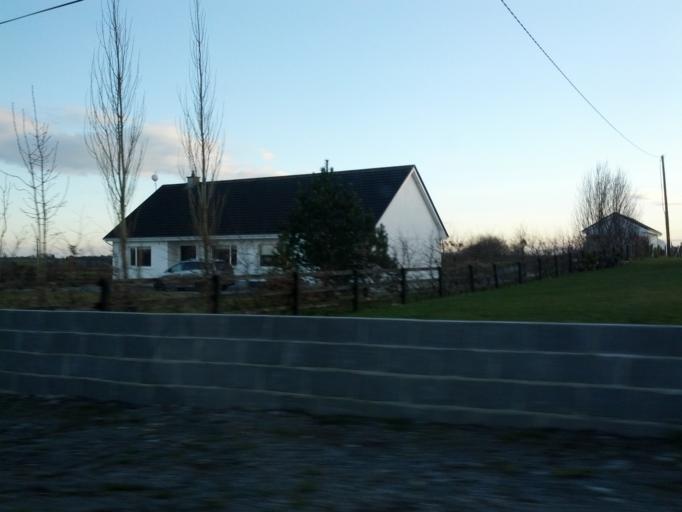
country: IE
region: Connaught
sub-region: County Galway
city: Athenry
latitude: 53.3276
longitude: -8.6385
